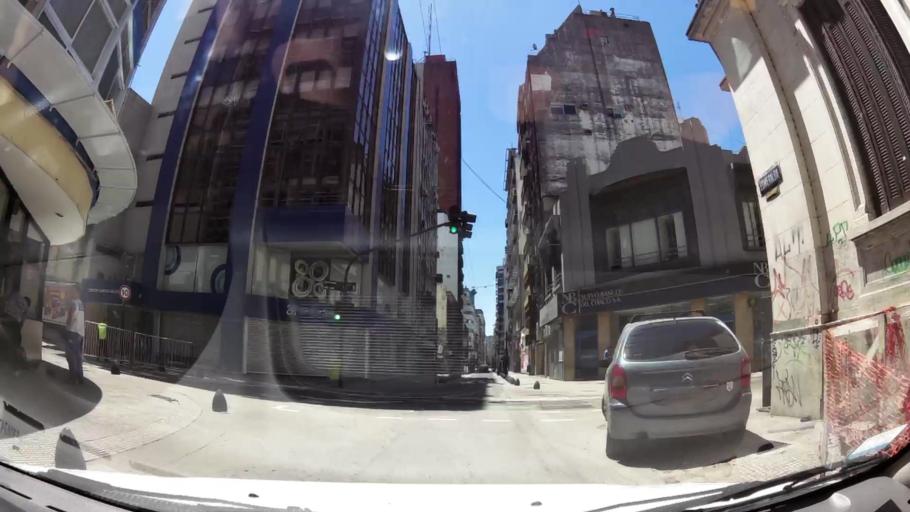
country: AR
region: Buenos Aires F.D.
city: Buenos Aires
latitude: -34.6048
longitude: -58.3781
